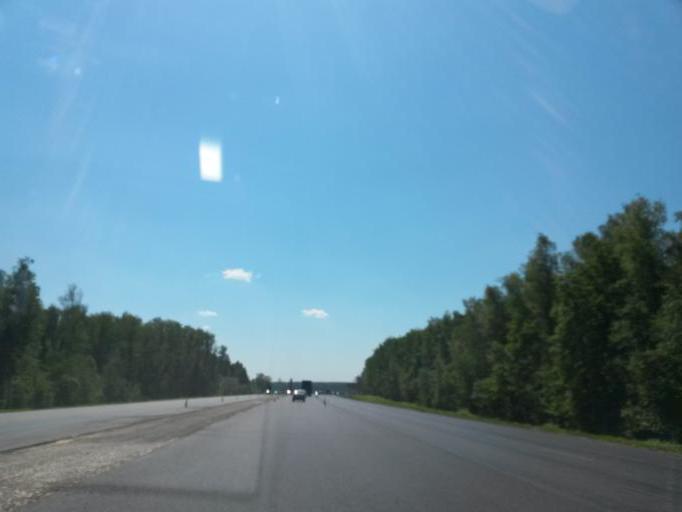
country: RU
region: Moskovskaya
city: Novyy Byt
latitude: 55.0962
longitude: 37.5852
